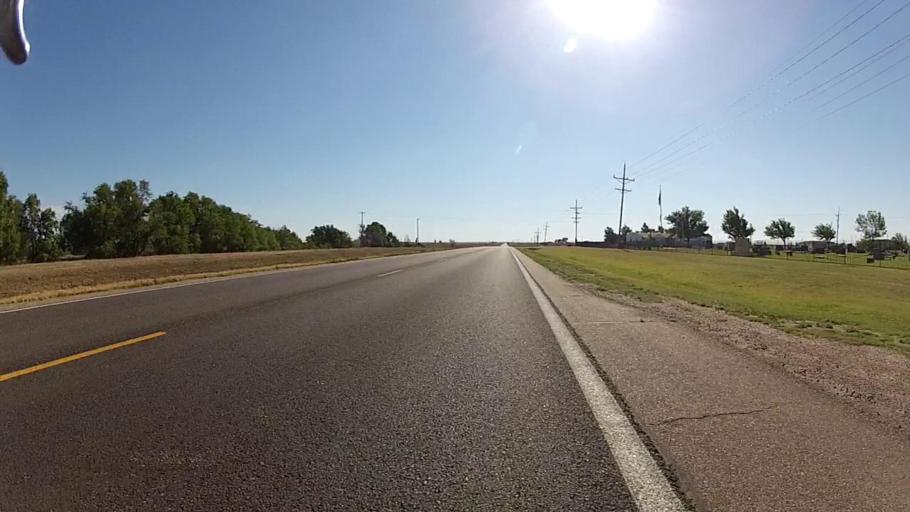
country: US
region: Kansas
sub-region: Haskell County
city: Sublette
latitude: 37.5462
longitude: -100.6172
